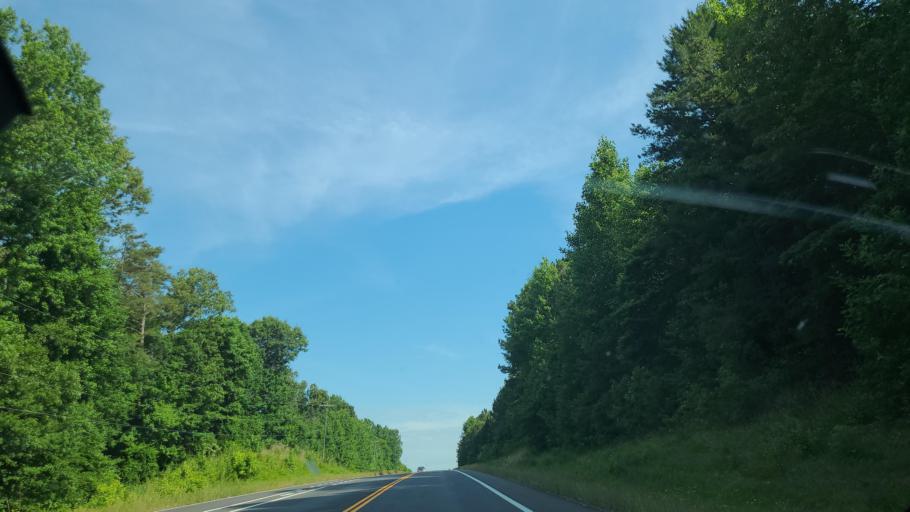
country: US
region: Georgia
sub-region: Franklin County
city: Gumlog
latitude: 34.5062
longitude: -83.0415
